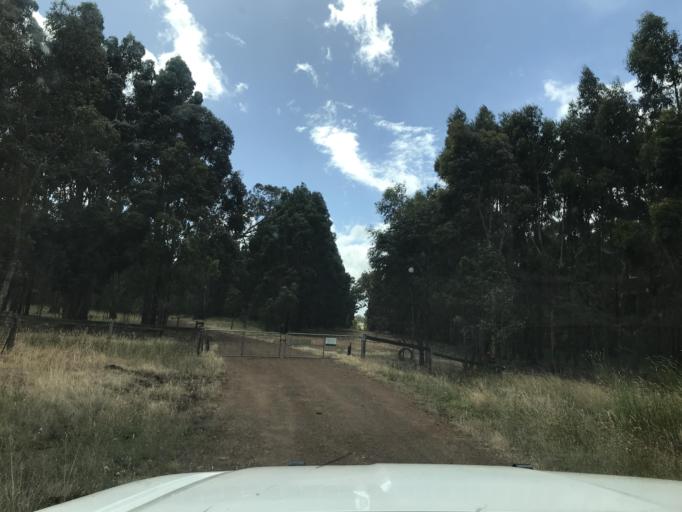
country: AU
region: South Australia
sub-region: Wattle Range
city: Penola
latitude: -37.1917
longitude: 141.3966
